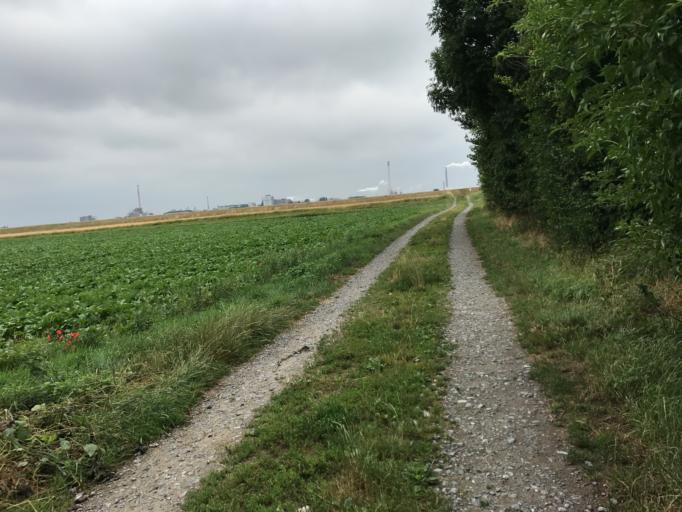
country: DE
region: North Rhine-Westphalia
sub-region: Regierungsbezirk Dusseldorf
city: Hochfeld
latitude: 51.3614
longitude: 6.6829
